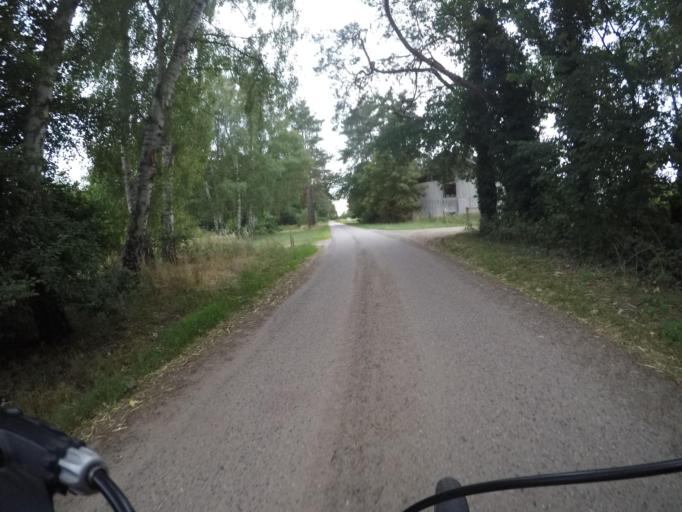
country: DE
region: Lower Saxony
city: Neu Darchau
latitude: 53.2562
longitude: 10.9538
